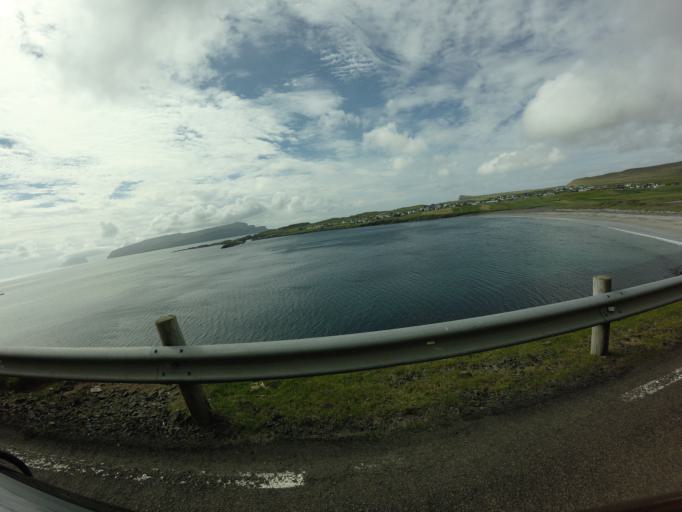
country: FO
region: Sandoy
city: Sandur
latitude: 61.8372
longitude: -6.8005
